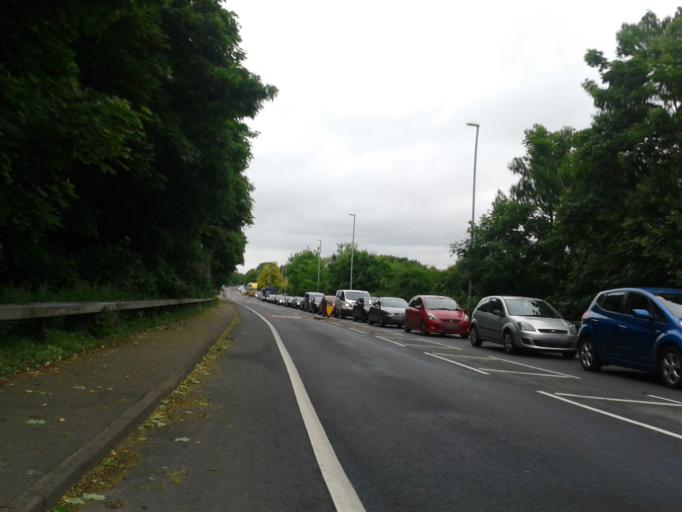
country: GB
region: England
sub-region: Cambridgeshire
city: Histon
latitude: 52.2424
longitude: 0.1128
